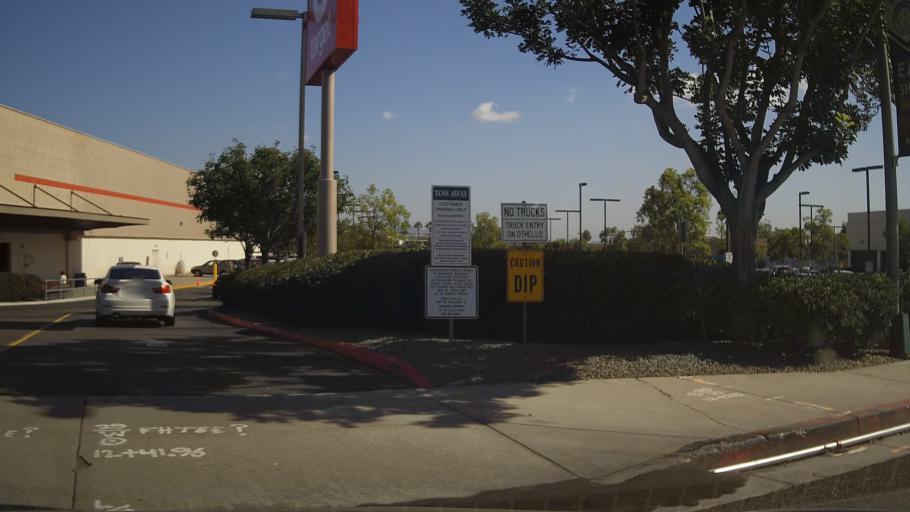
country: US
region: California
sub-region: San Diego County
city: San Diego
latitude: 32.8160
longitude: -117.1546
